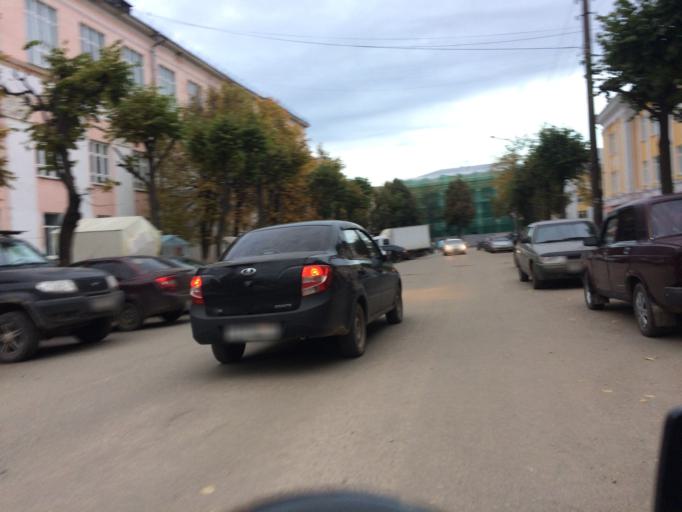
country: RU
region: Mariy-El
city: Yoshkar-Ola
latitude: 56.6330
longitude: 47.8884
